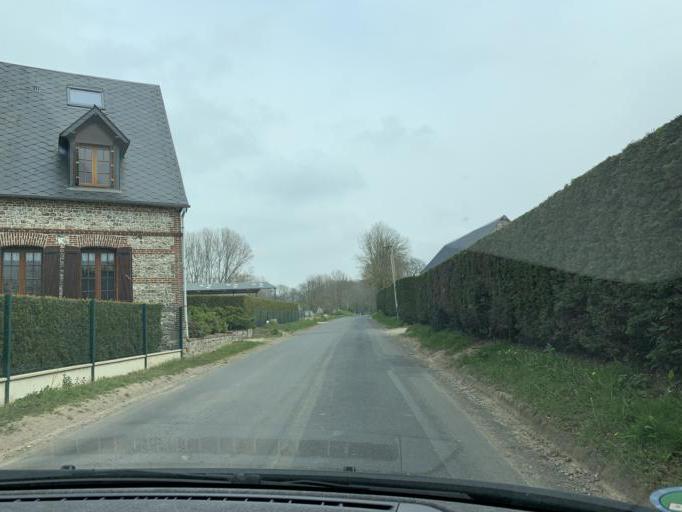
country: FR
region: Haute-Normandie
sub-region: Departement de la Seine-Maritime
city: Saint-Valery-en-Caux
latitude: 49.8581
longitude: 0.7525
